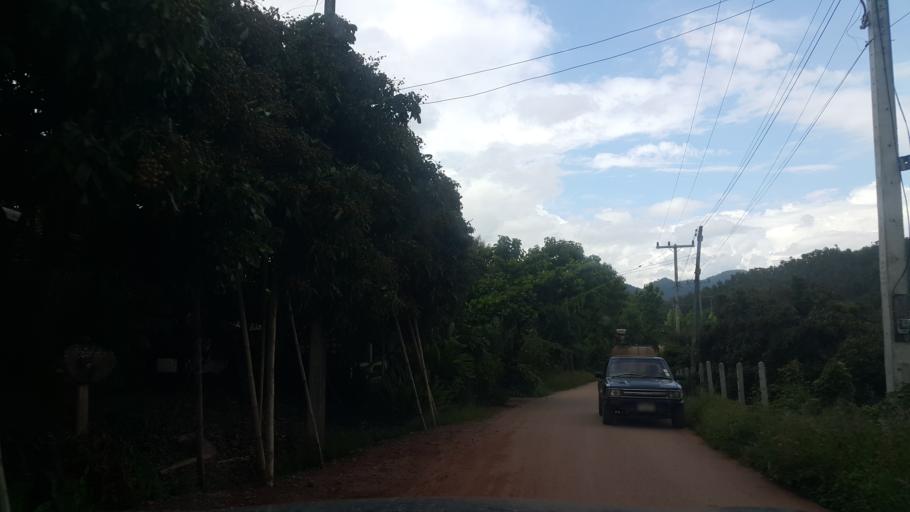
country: TH
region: Chiang Mai
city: Mae Taeng
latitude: 19.2178
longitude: 99.0110
